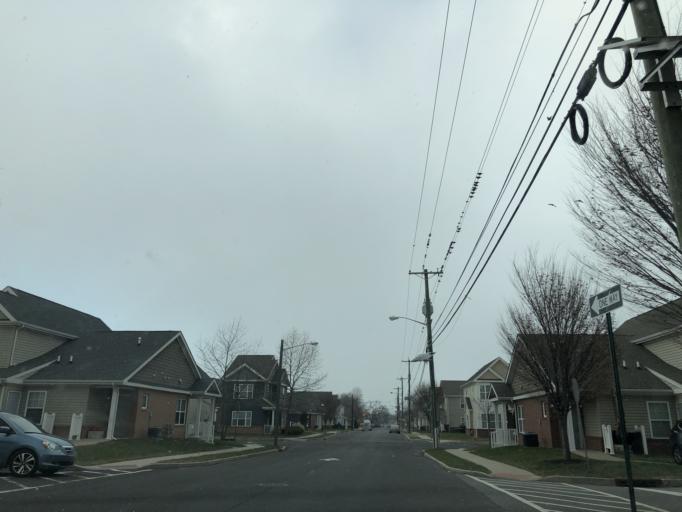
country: US
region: New Jersey
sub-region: Camden County
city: Camden
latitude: 39.9216
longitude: -75.1122
